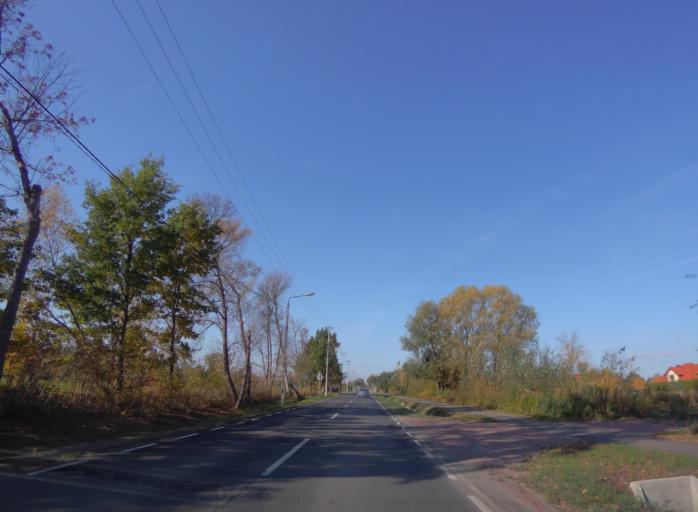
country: PL
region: Masovian Voivodeship
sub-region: Powiat minski
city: Halinow
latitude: 52.1897
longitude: 21.3390
